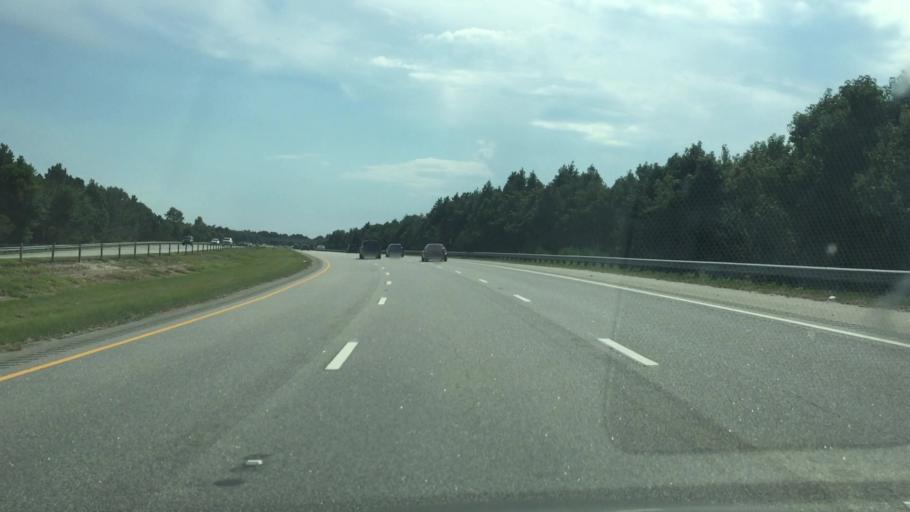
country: US
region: South Carolina
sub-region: Horry County
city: North Myrtle Beach
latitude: 33.8241
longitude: -78.7346
